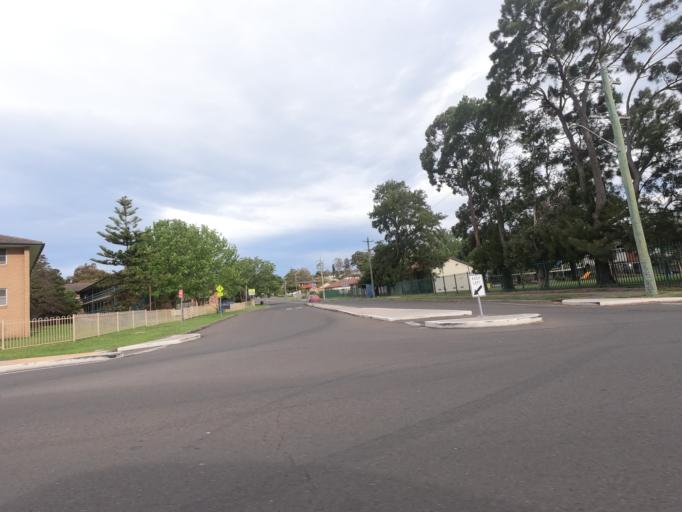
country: AU
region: New South Wales
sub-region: Wollongong
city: Berkeley
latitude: -34.4746
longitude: 150.8410
